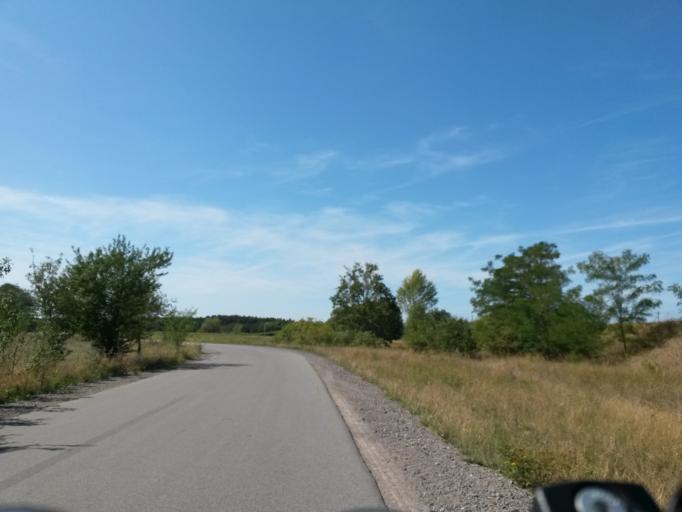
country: DE
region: Saxony-Anhalt
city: Hassel
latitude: 52.5970
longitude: 11.9533
